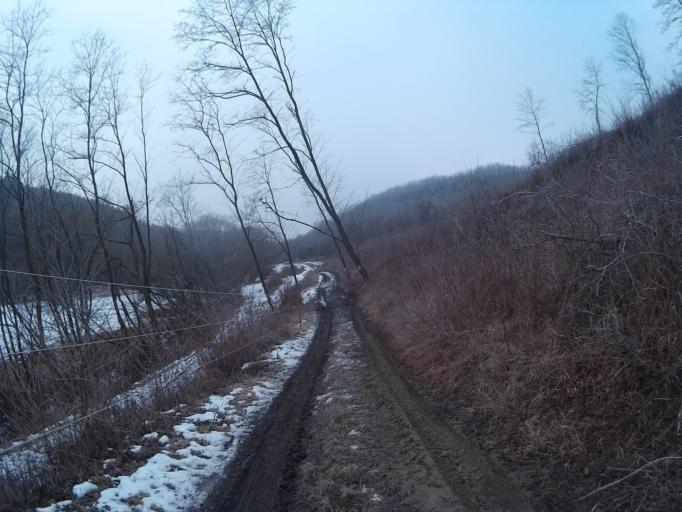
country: HU
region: Nograd
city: Tar
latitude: 47.9937
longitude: 19.7387
